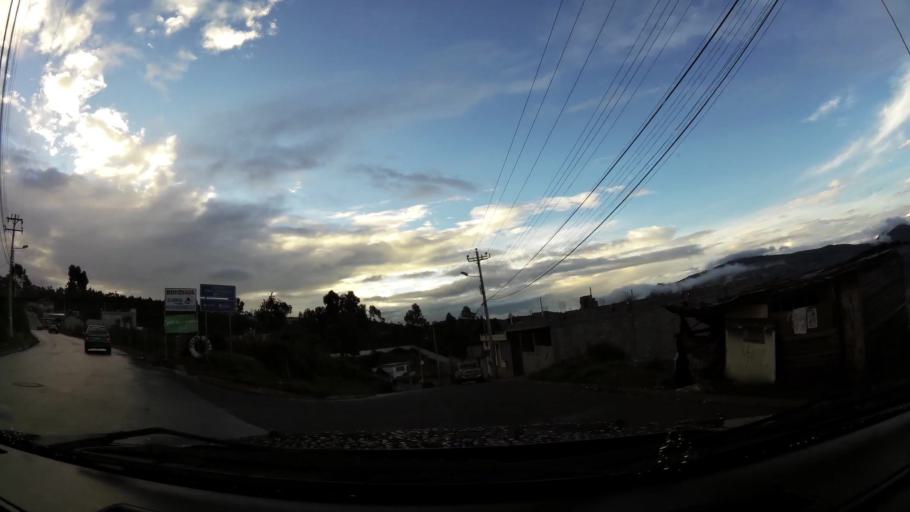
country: EC
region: Pichincha
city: Quito
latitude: -0.1047
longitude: -78.5249
